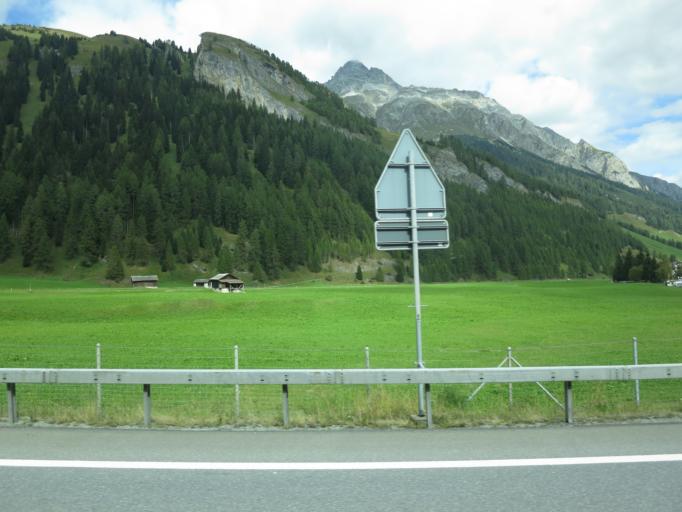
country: CH
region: Grisons
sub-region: Hinterrhein District
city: Hinterrhein
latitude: 46.5468
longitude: 9.3108
